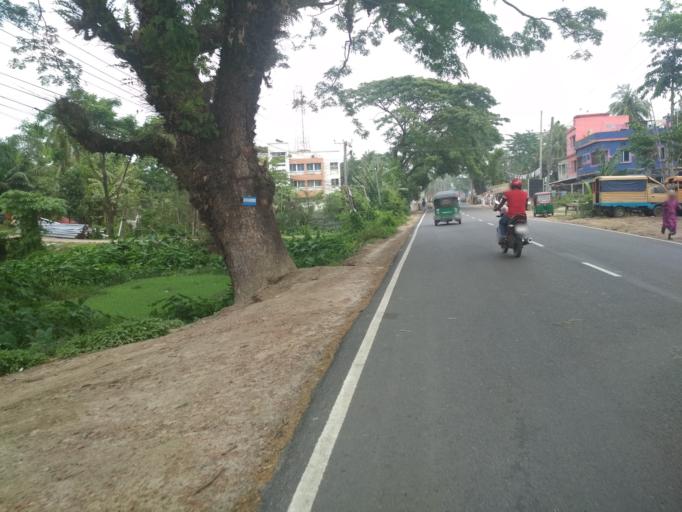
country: BD
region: Chittagong
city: Lakshmipur
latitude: 22.9421
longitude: 90.8456
